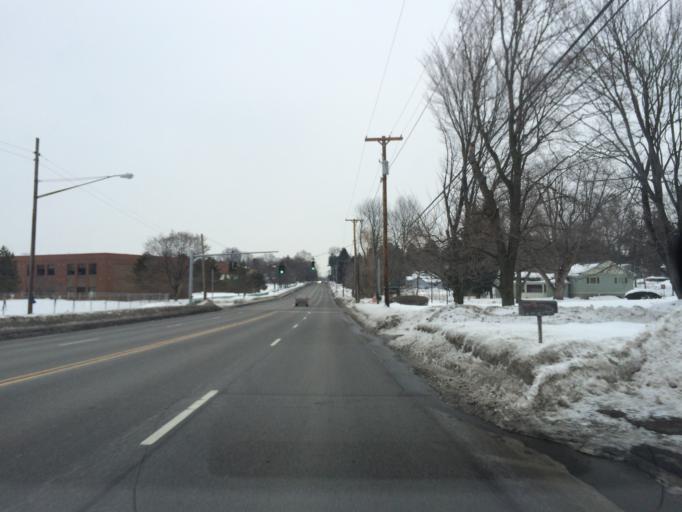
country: US
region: New York
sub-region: Monroe County
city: East Rochester
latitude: 43.1069
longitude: -77.4957
